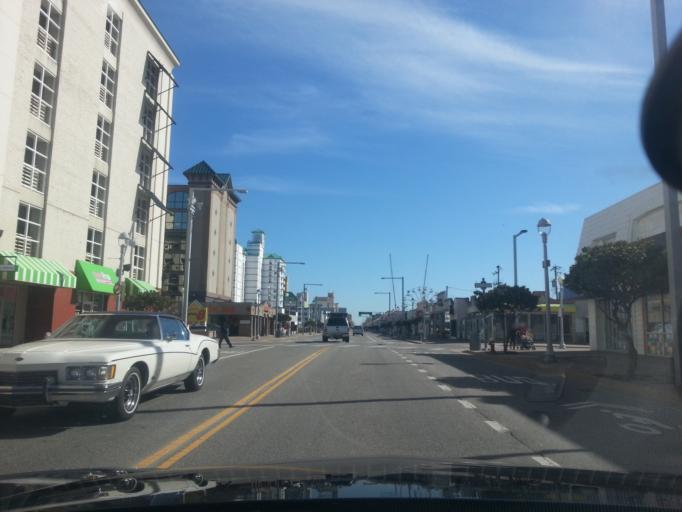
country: US
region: Virginia
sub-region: City of Virginia Beach
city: Virginia Beach
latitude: 36.8468
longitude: -75.9746
